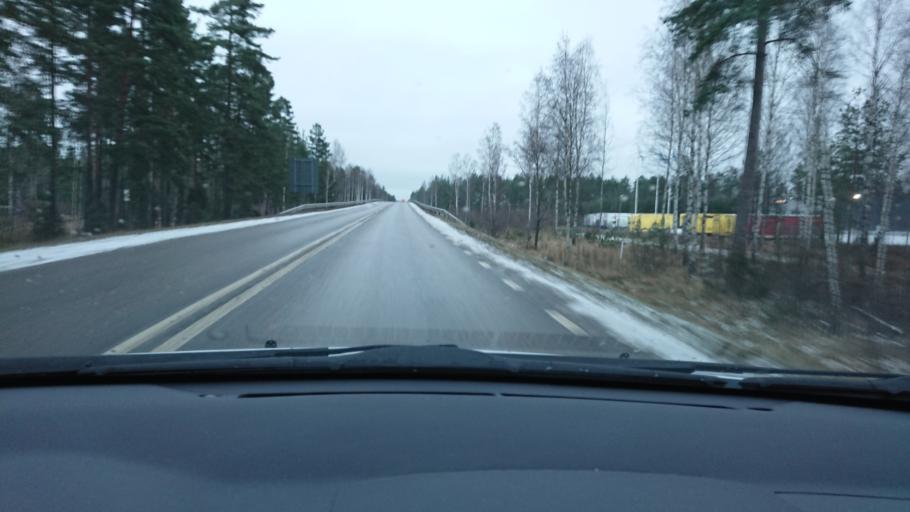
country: SE
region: Kalmar
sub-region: Hultsfreds Kommun
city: Hultsfred
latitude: 57.5027
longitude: 15.8242
